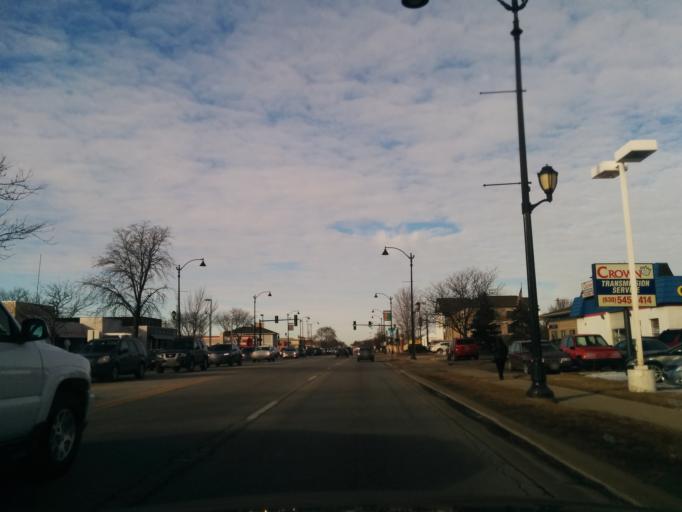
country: US
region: Illinois
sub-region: DuPage County
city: Glen Ellyn
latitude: 41.8594
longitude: -88.0658
